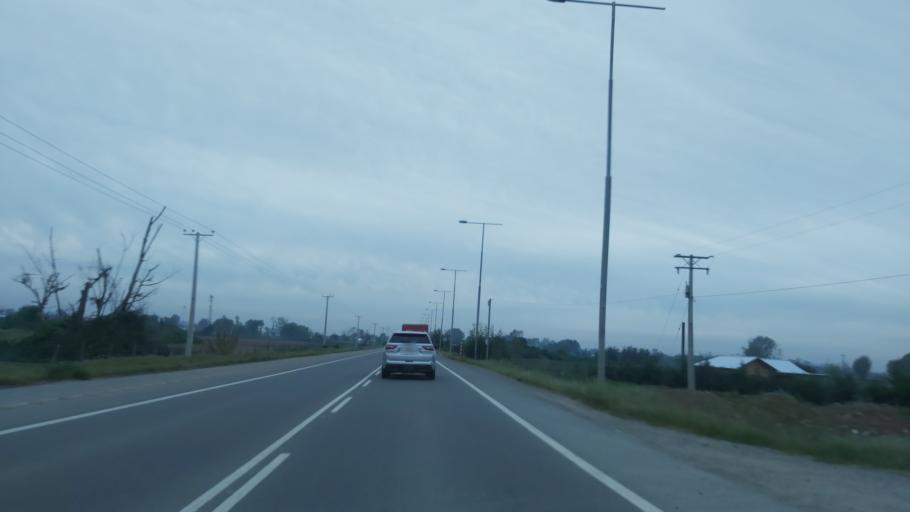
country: CL
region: Maule
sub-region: Provincia de Linares
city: Linares
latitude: -35.8274
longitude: -71.6052
